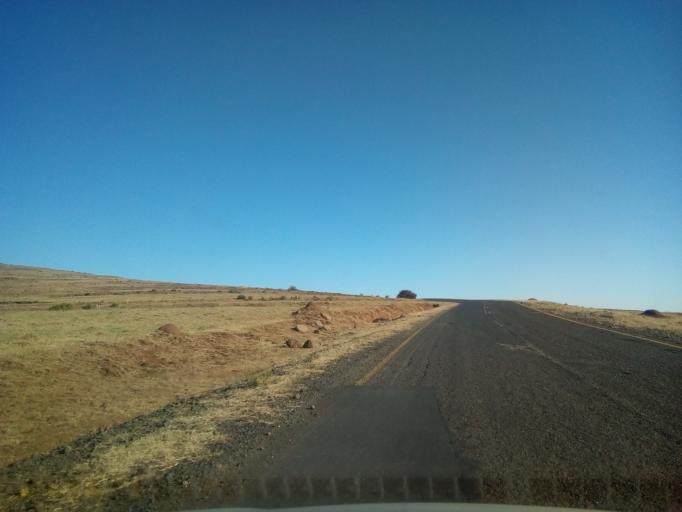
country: LS
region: Berea
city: Teyateyaneng
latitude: -29.2541
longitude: 27.7736
